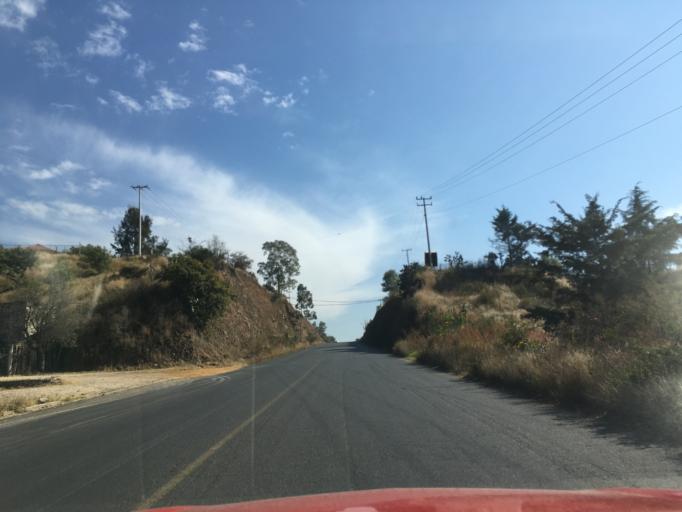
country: MX
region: Michoacan
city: Ciudad Hidalgo
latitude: 19.7074
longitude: -100.5538
